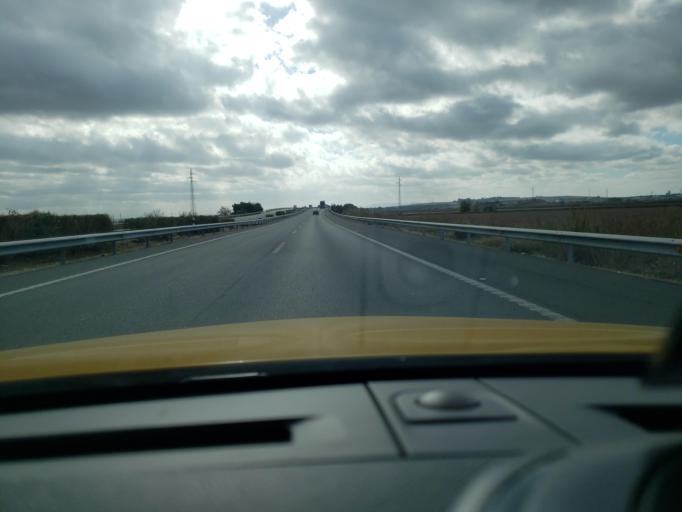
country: ES
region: Andalusia
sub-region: Provincia de Sevilla
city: Las Cabezas de San Juan
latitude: 37.0388
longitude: -5.9274
